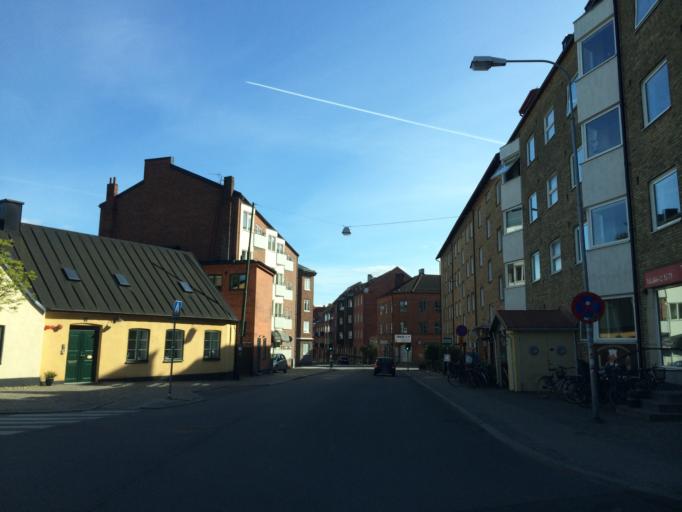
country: SE
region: Skane
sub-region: Lunds Kommun
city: Lund
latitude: 55.7004
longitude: 13.1955
